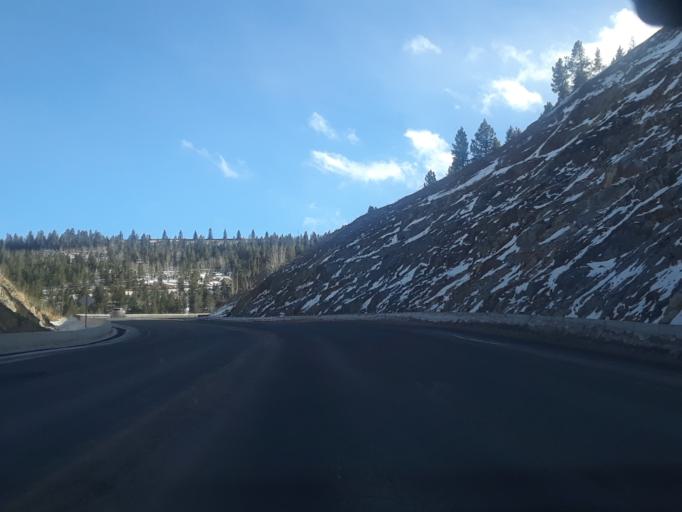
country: US
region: Colorado
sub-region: Gilpin County
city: Central City
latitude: 39.7954
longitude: -105.5162
